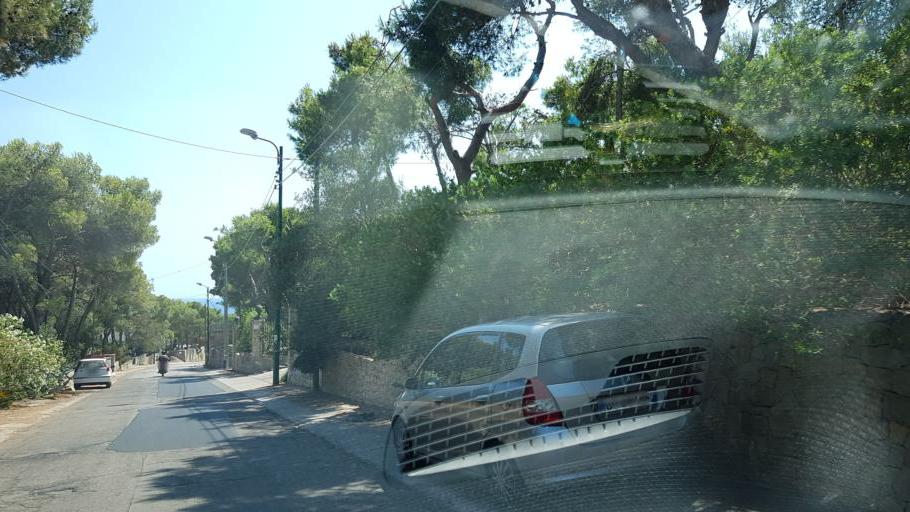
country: IT
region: Apulia
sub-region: Provincia di Lecce
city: Nardo
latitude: 40.1433
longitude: 17.9838
